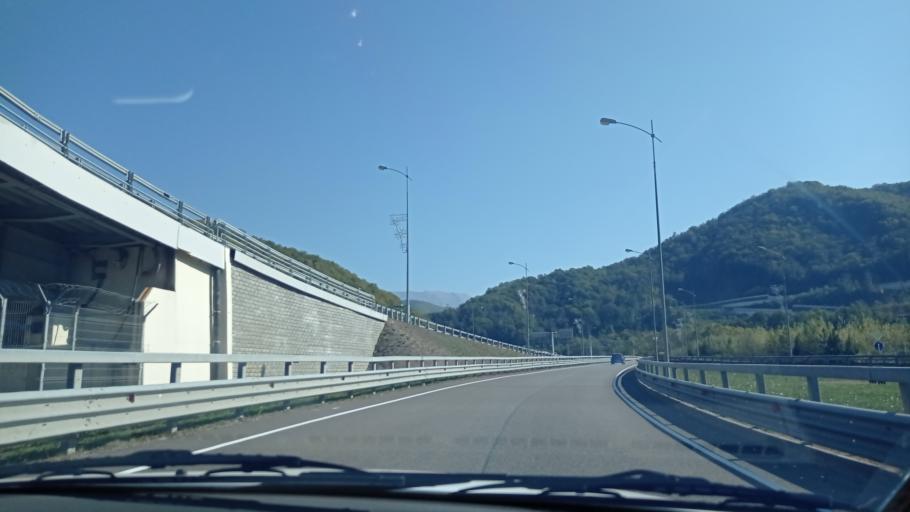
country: RU
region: Krasnodarskiy
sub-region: Sochi City
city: Krasnaya Polyana
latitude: 43.6865
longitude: 40.2342
